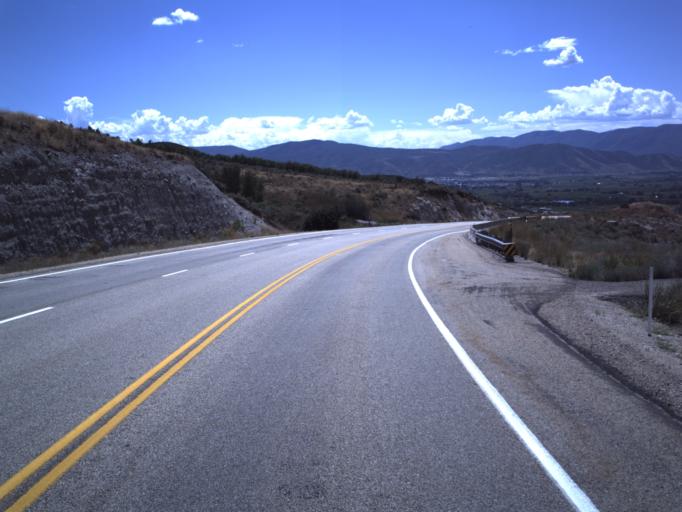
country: US
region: Utah
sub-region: Wasatch County
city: Heber
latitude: 40.5853
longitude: -111.4203
